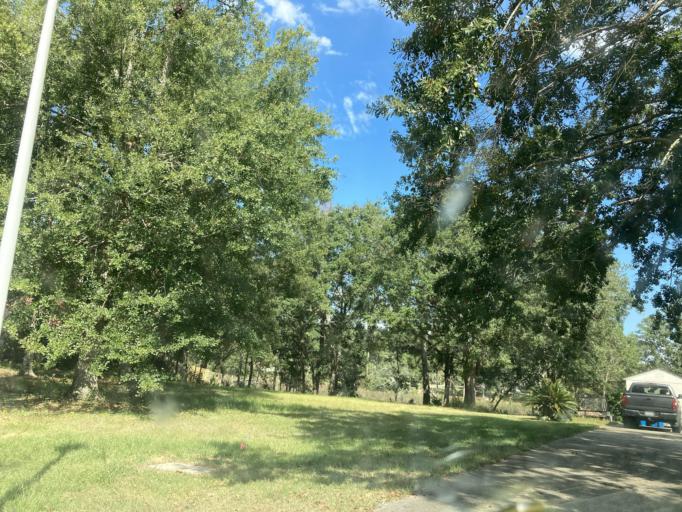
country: US
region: Mississippi
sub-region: Jackson County
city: Gulf Hills
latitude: 30.4386
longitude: -88.8514
